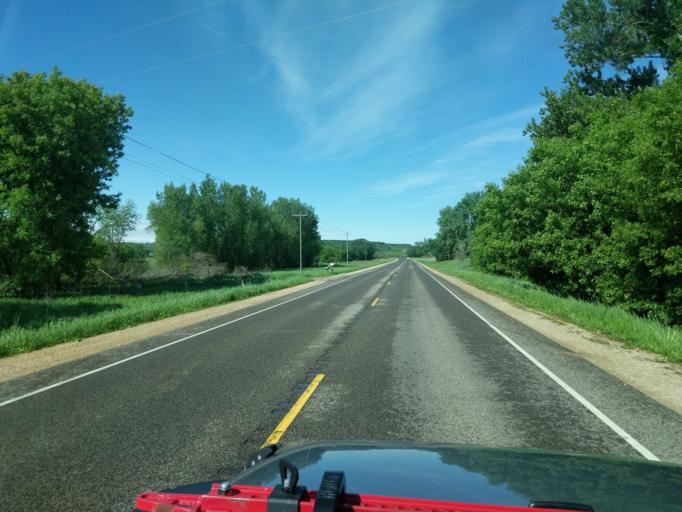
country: US
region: Wisconsin
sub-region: Pierce County
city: River Falls
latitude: 44.8540
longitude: -92.5422
